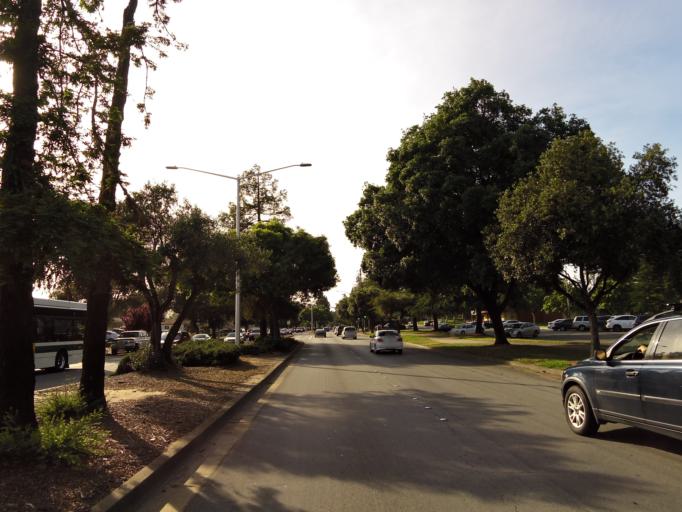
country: US
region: California
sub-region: Alameda County
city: Fremont
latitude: 37.5444
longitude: -121.9643
